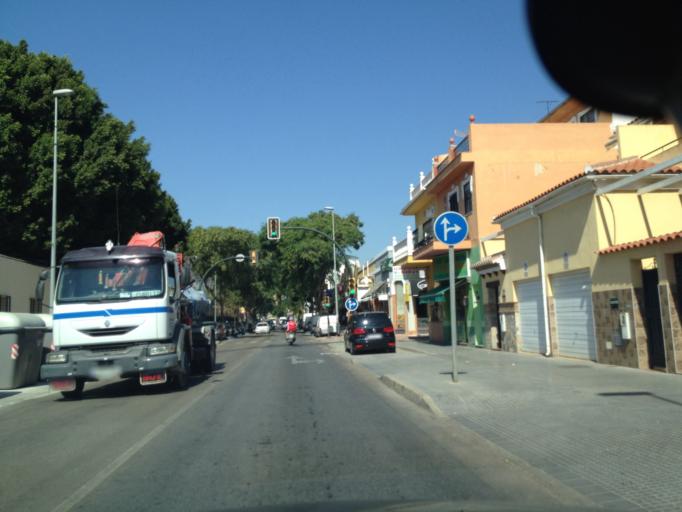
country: ES
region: Andalusia
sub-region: Provincia de Malaga
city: Alhaurin de la Torre
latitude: 36.7230
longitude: -4.5377
